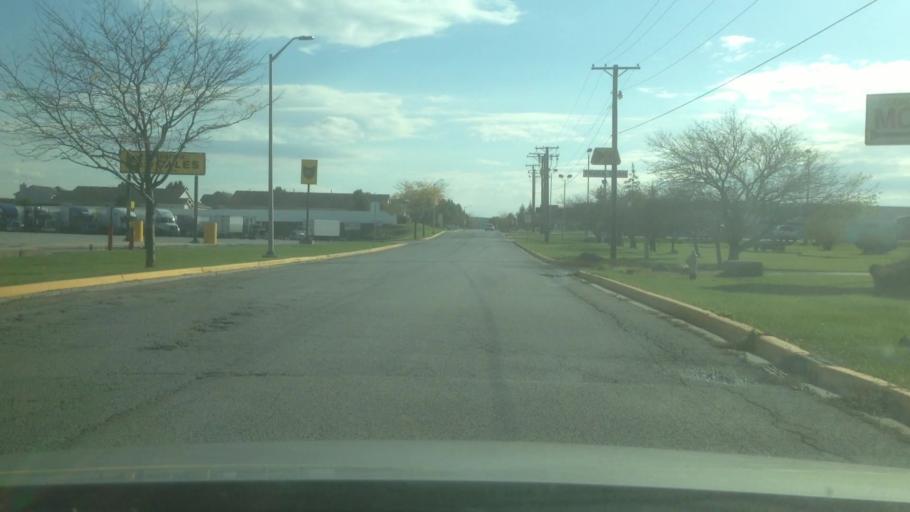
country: US
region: Illinois
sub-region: Will County
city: Monee
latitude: 41.4260
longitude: -87.7564
